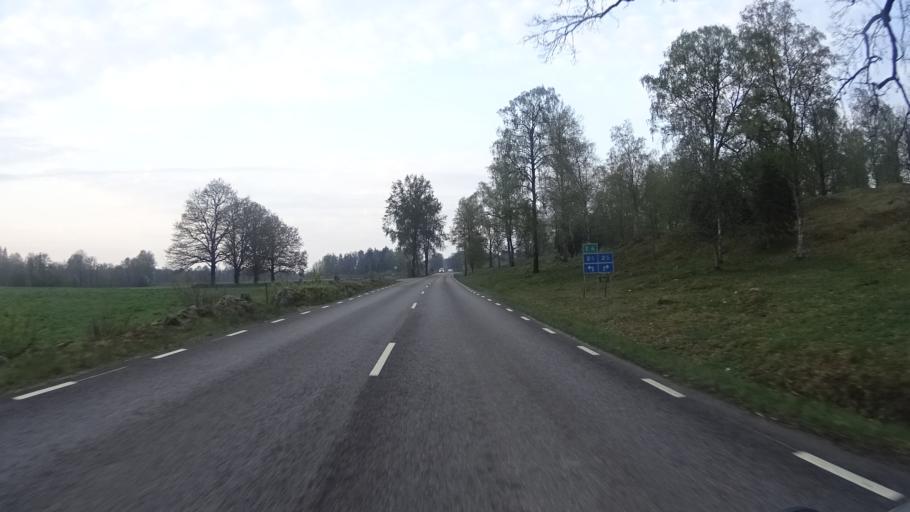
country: SE
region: Kronoberg
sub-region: Ljungby Kommun
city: Ljungby
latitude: 56.8468
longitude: 13.9744
